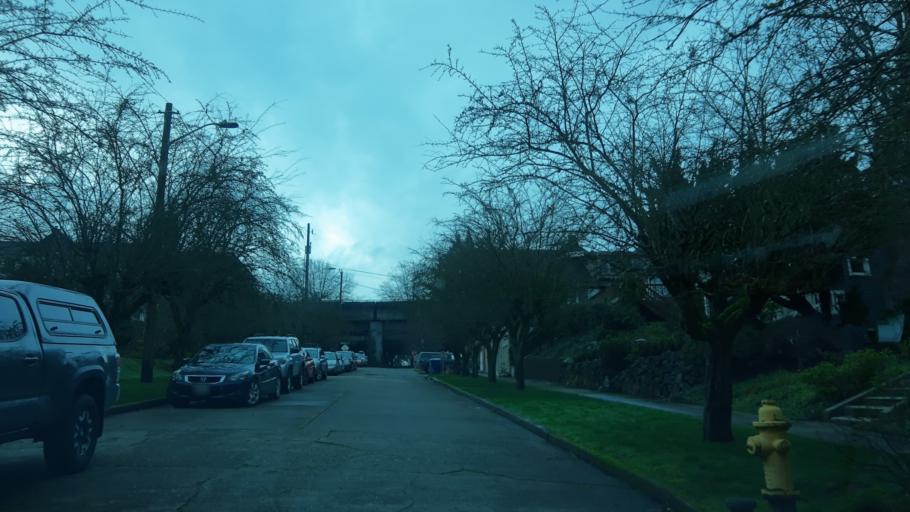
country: US
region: Washington
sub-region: King County
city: Seattle
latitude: 47.6478
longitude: -122.3207
